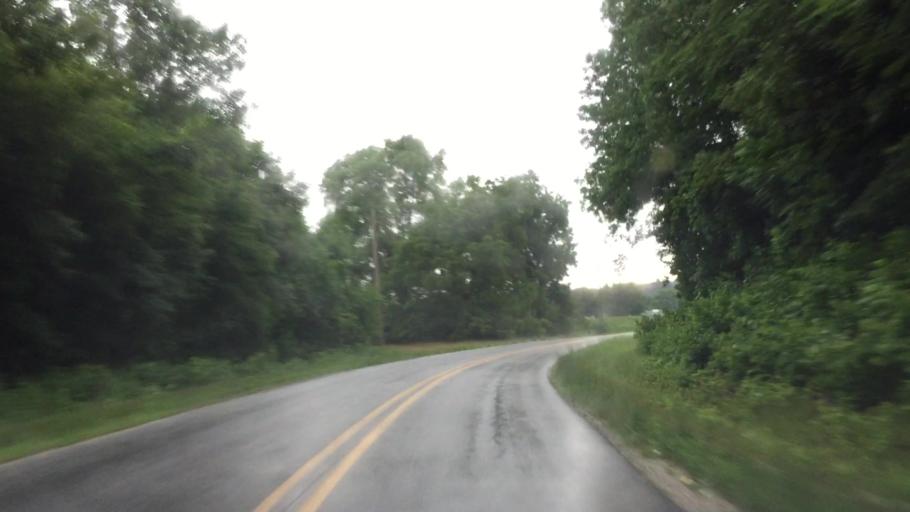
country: US
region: Iowa
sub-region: Lee County
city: Fort Madison
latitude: 40.6113
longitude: -91.2817
